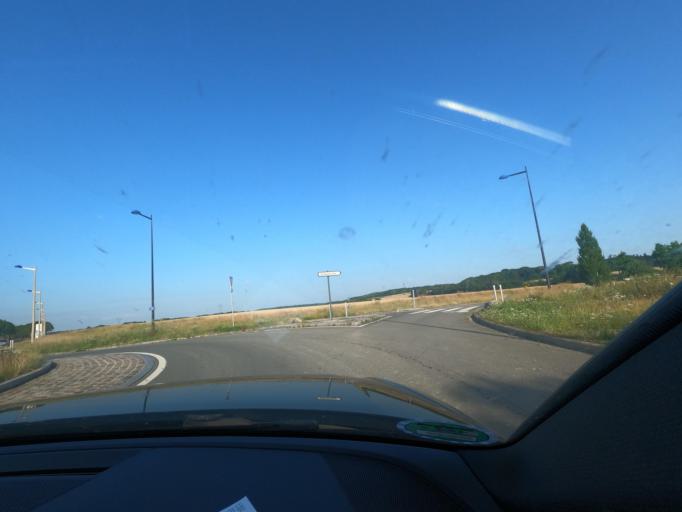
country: FR
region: Picardie
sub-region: Departement de la Somme
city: Pont-de-Metz
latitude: 49.8986
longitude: 2.2514
